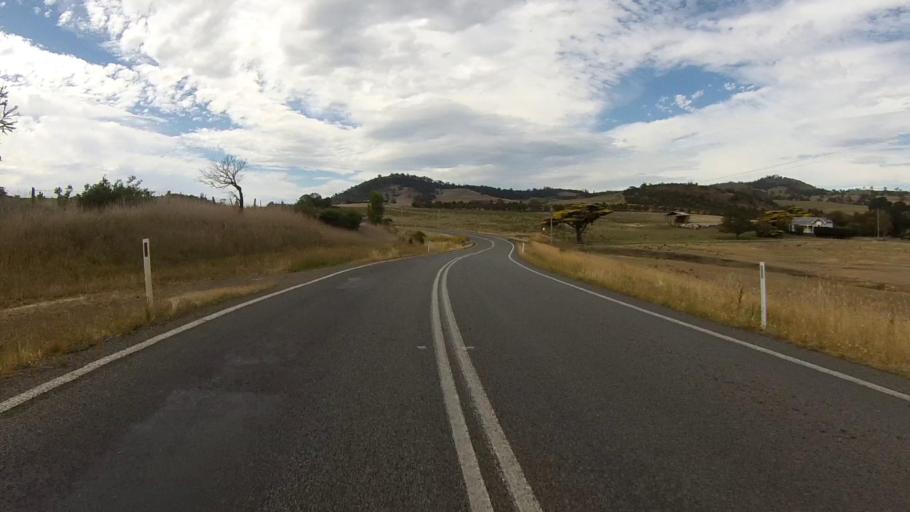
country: AU
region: Tasmania
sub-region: Sorell
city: Sorell
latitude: -42.6933
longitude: 147.4763
